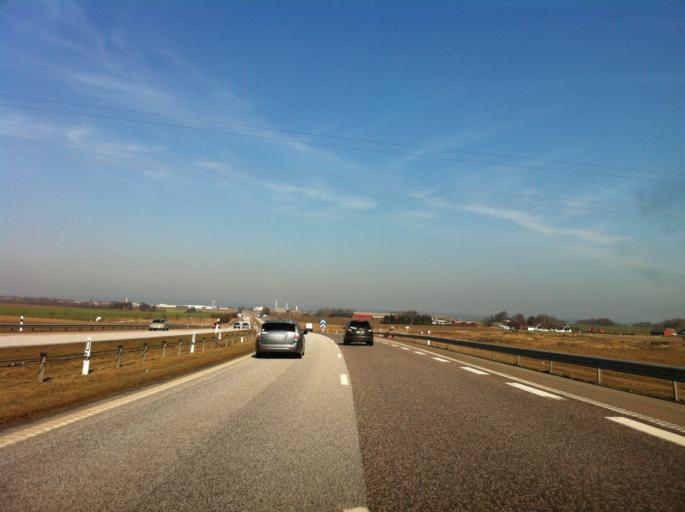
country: SE
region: Skane
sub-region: Angelholms Kommun
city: AEngelholm
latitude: 56.2225
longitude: 12.8971
